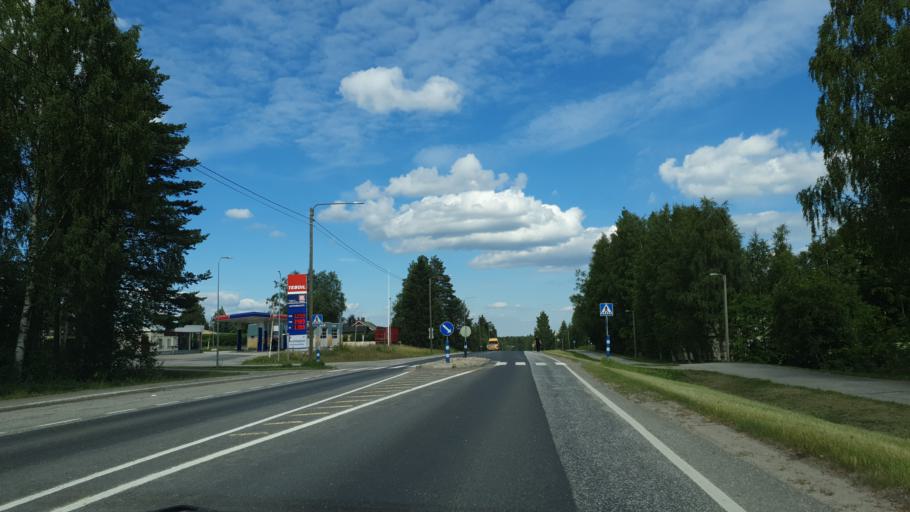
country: FI
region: Kainuu
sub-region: Kajaani
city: Kajaani
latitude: 64.2403
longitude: 27.7529
